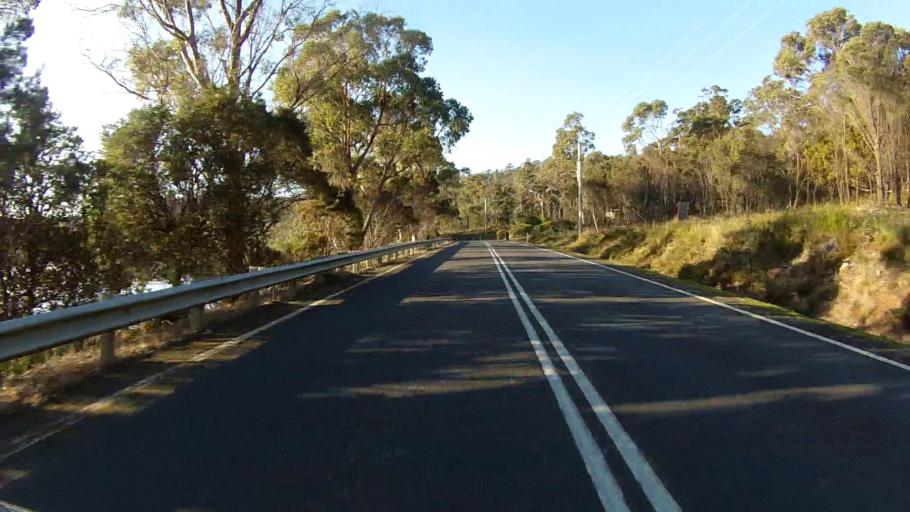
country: AU
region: Tasmania
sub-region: Clarence
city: Sandford
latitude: -43.0333
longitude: 147.8669
